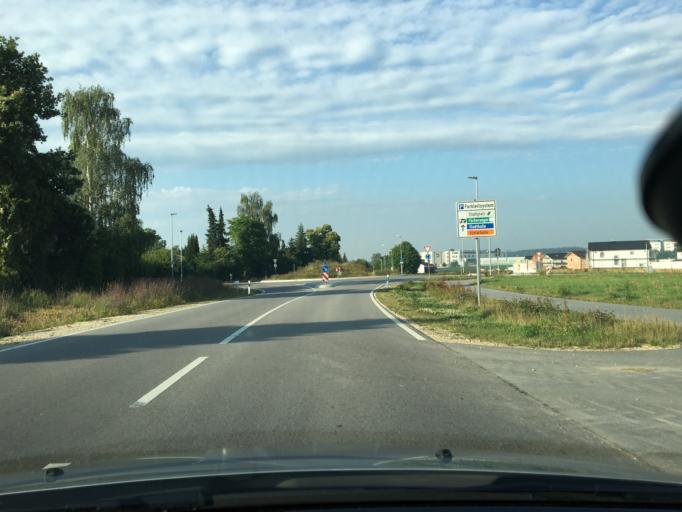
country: DE
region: Bavaria
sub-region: Lower Bavaria
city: Vilsbiburg
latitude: 48.4604
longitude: 12.3499
